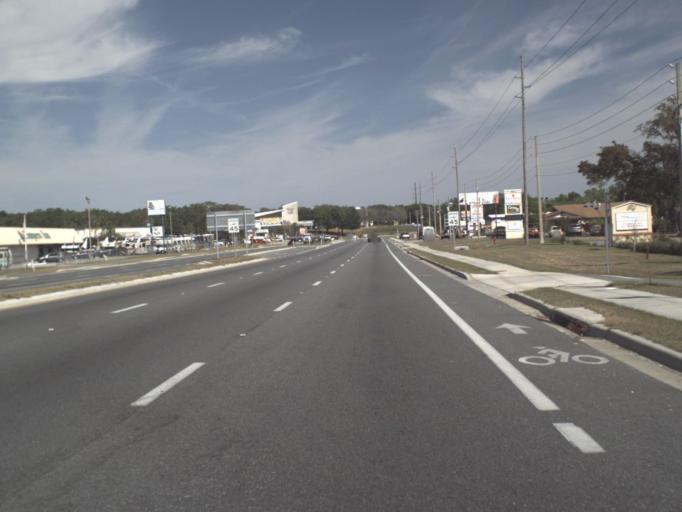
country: US
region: Florida
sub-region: Lake County
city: Fruitland Park
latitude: 28.8508
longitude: -81.9008
